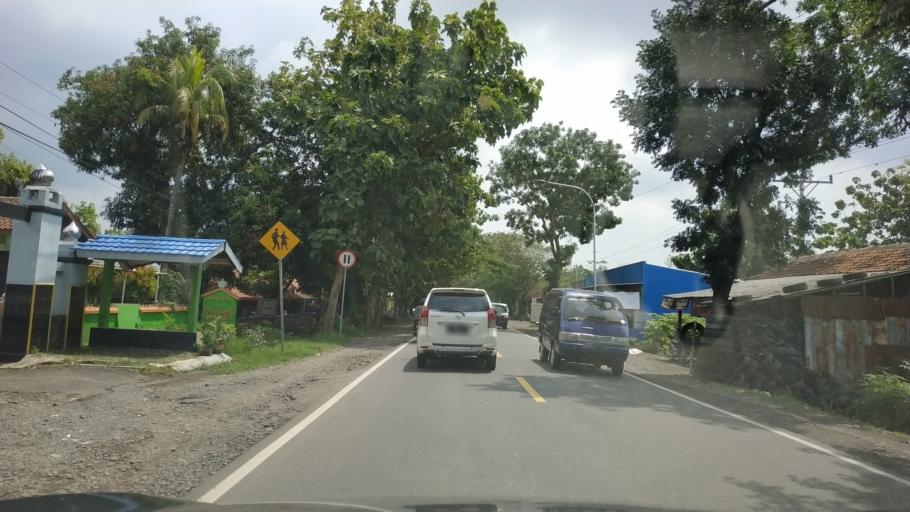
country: ID
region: Central Java
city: Slawi
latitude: -7.0119
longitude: 109.1415
